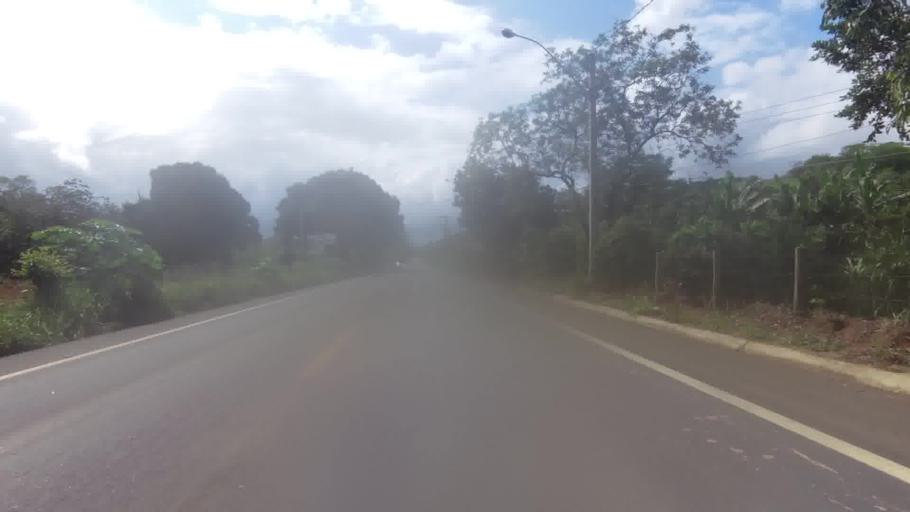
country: BR
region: Espirito Santo
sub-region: Piuma
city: Piuma
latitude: -20.8133
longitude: -40.6855
